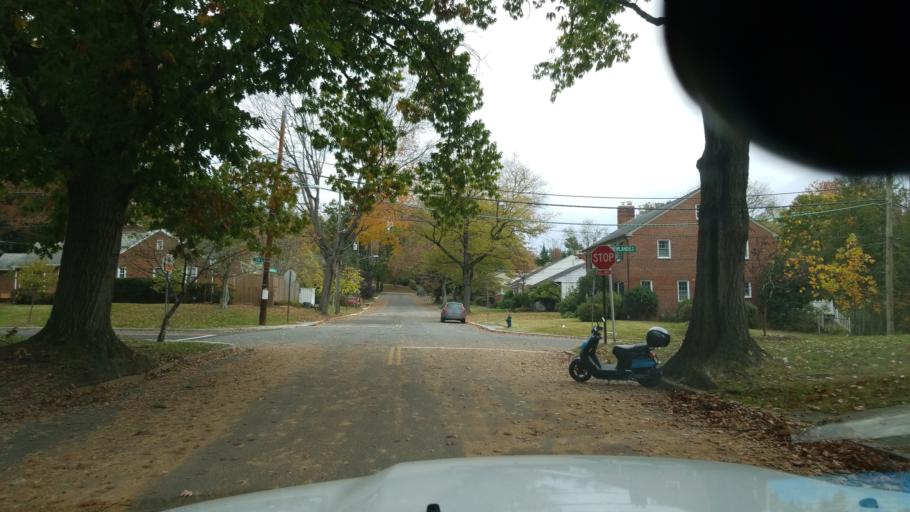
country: US
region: Maryland
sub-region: Montgomery County
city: Chevy Chase
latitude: 38.9635
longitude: -77.0589
